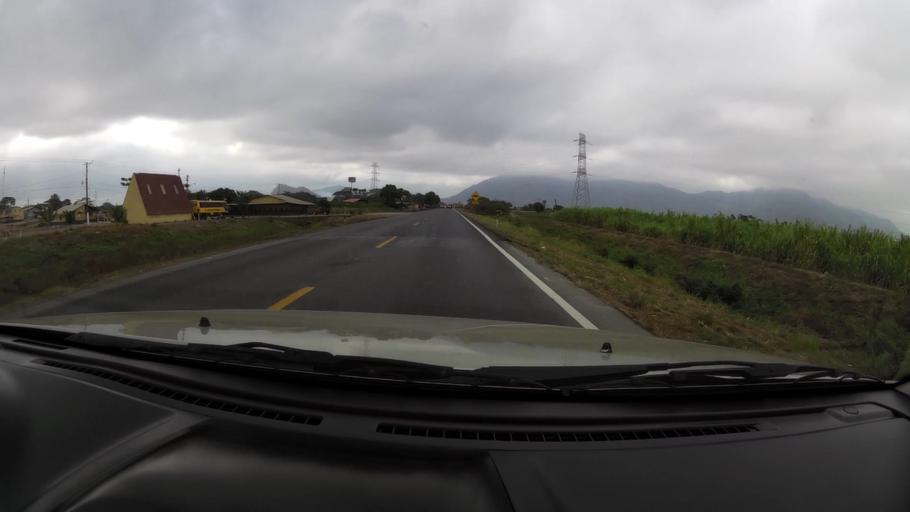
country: EC
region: Guayas
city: Coronel Marcelino Mariduena
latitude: -2.3463
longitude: -79.6345
